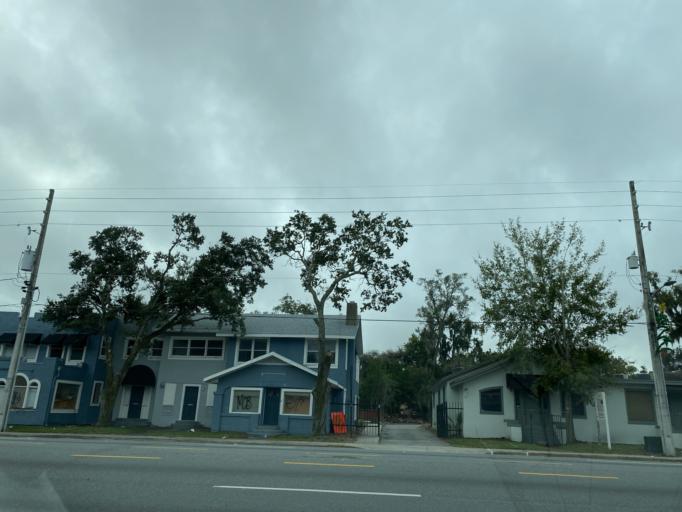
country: US
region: Florida
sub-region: Orange County
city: Orlando
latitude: 28.5532
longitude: -81.3899
